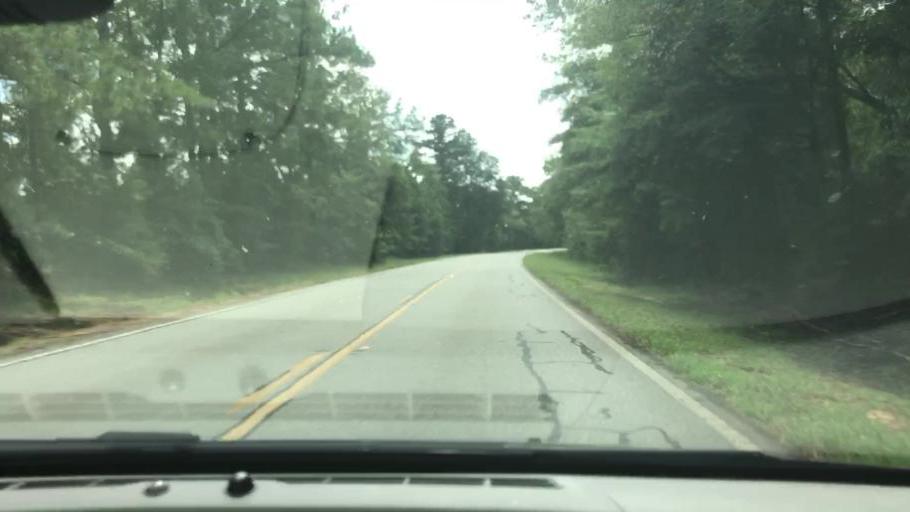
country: US
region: Georgia
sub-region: Quitman County
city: Georgetown
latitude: 32.0987
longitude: -85.0388
